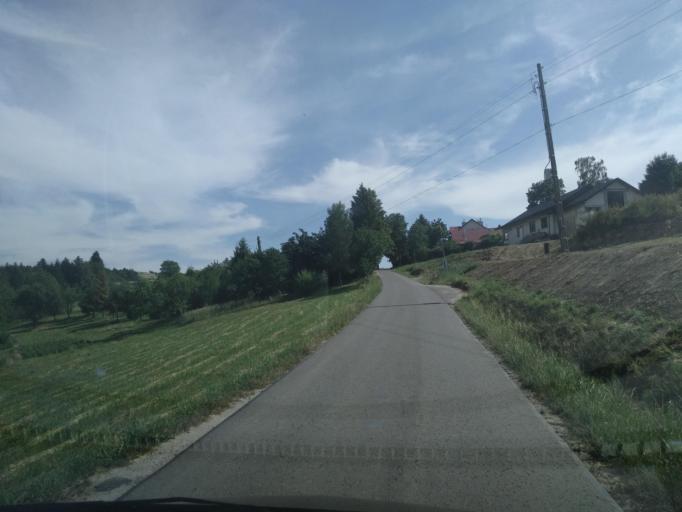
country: PL
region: Subcarpathian Voivodeship
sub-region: Powiat krosnienski
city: Iwonicz-Zdroj
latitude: 49.5461
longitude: 21.7780
